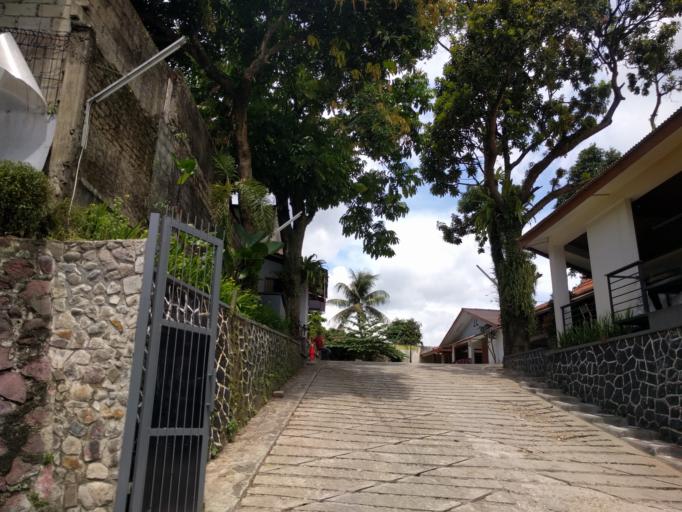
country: ID
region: West Java
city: Bogor
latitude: -6.6178
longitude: 106.8151
